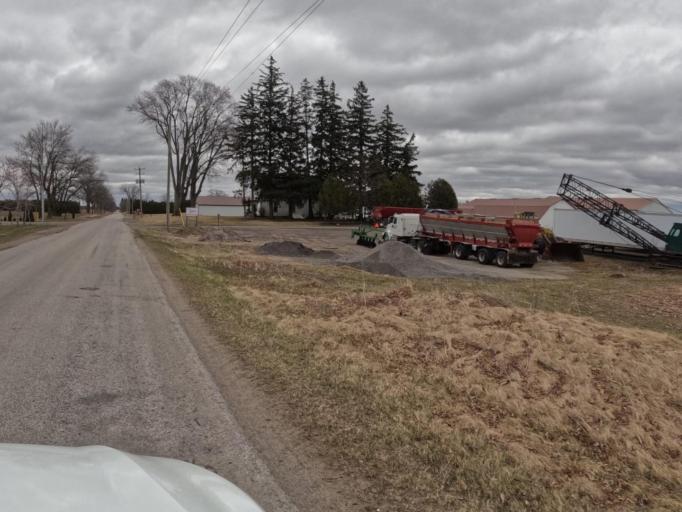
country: CA
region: Ontario
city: Norfolk County
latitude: 42.9422
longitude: -80.4103
